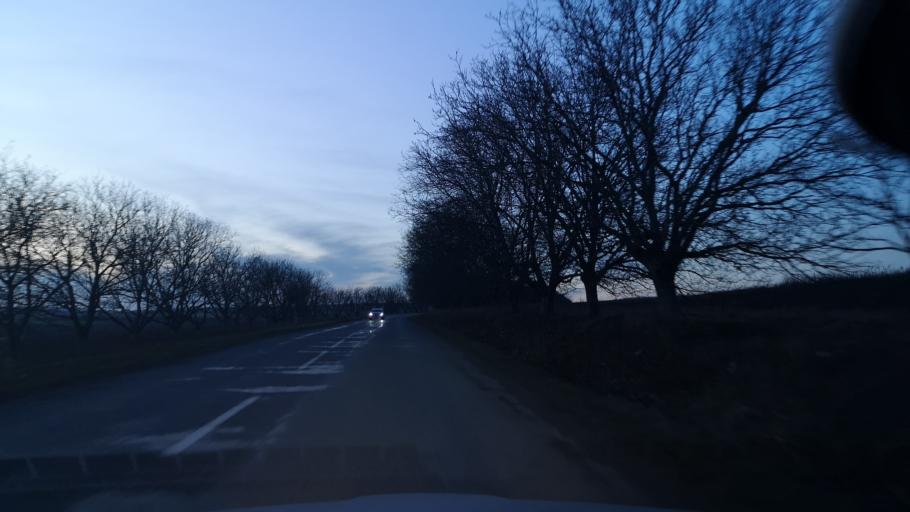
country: MD
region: Orhei
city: Orhei
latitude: 47.2851
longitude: 28.8282
